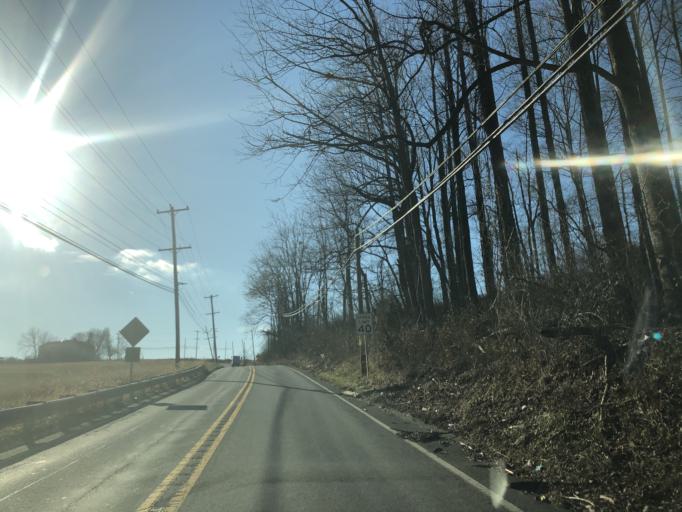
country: US
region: Pennsylvania
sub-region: Chester County
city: South Coatesville
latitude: 39.9679
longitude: -75.8338
